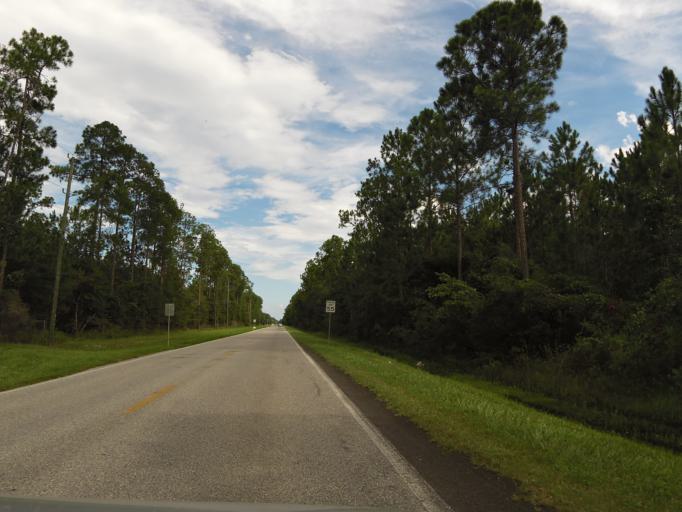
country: US
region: Florida
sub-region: Clay County
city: Asbury Lake
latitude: 30.0520
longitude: -81.7459
